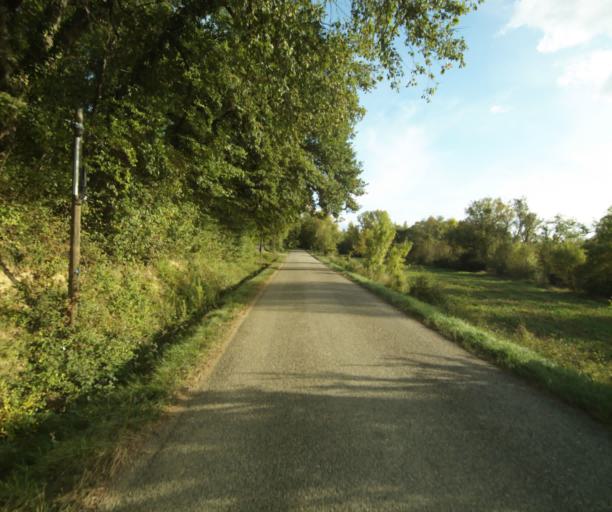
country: FR
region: Midi-Pyrenees
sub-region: Departement du Gers
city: Gondrin
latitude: 43.8939
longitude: 0.2970
